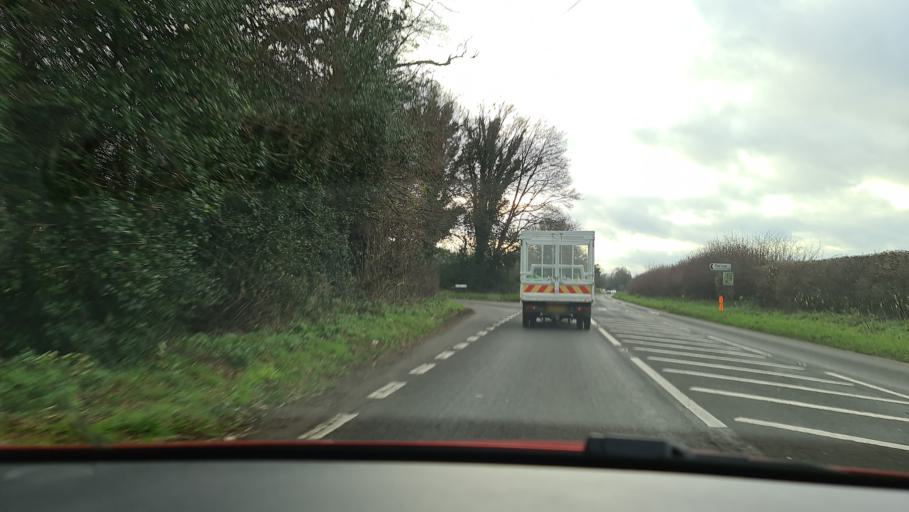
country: GB
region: England
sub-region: Buckinghamshire
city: Great Missenden
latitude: 51.7179
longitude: -0.7175
